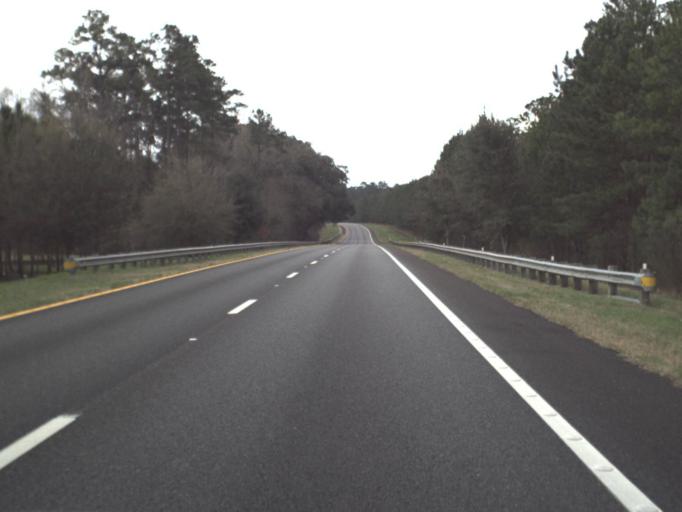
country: US
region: Georgia
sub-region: Grady County
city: Cairo
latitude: 30.6717
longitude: -84.1602
